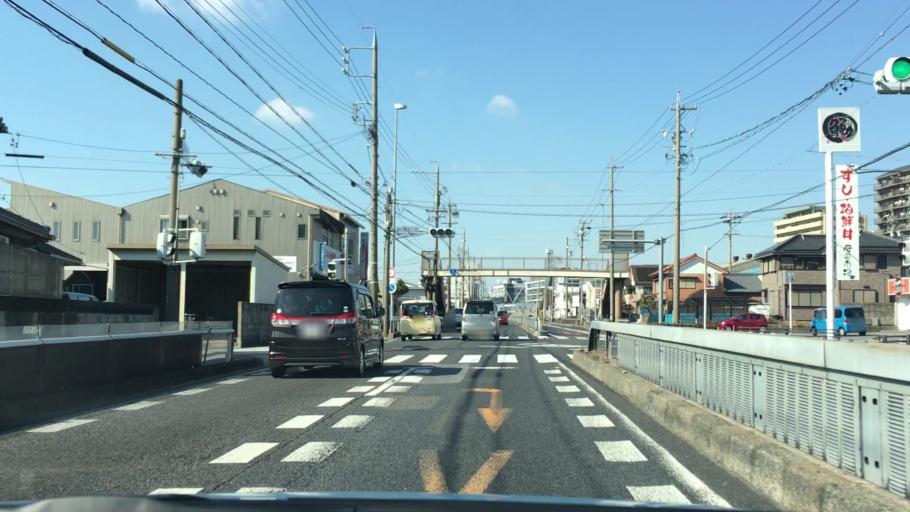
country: JP
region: Aichi
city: Okazaki
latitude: 34.9512
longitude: 137.1794
